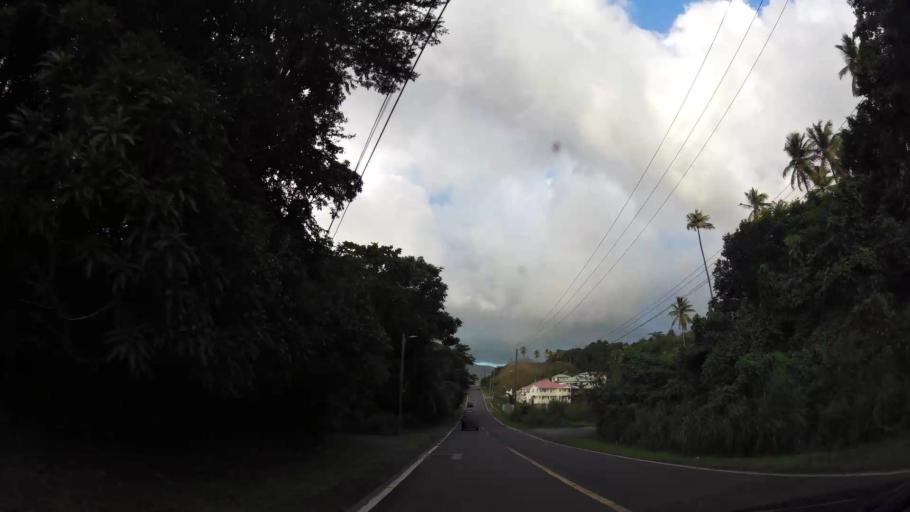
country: DM
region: Saint John
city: Portsmouth
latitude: 15.5478
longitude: -61.4642
